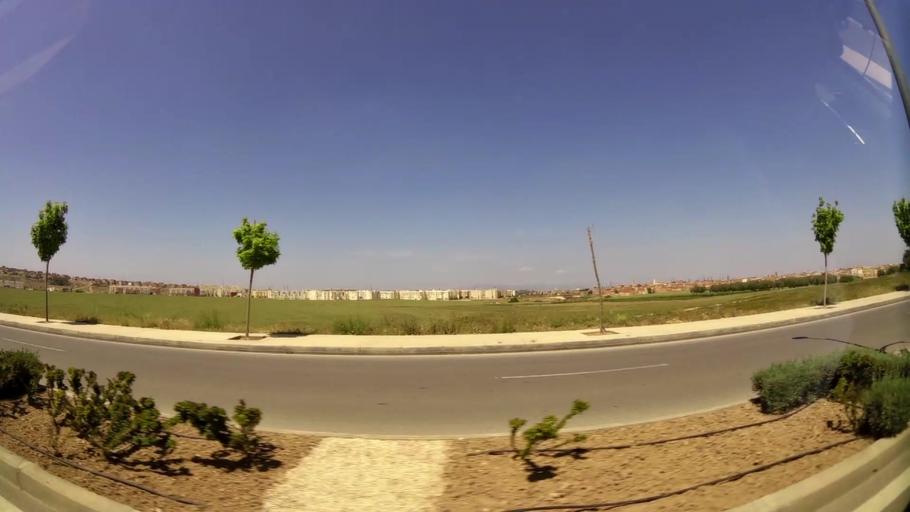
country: MA
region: Oriental
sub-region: Oujda-Angad
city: Oujda
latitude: 34.6954
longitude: -1.9311
